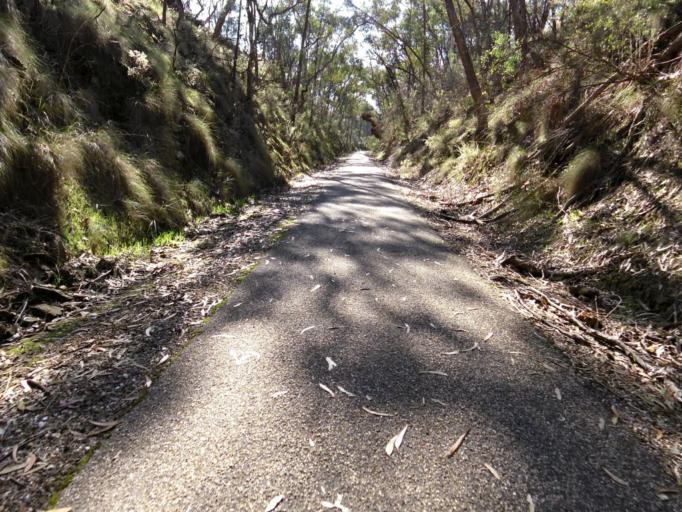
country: AU
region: Victoria
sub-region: Wangaratta
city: Wangaratta
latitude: -36.4088
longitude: 146.6161
